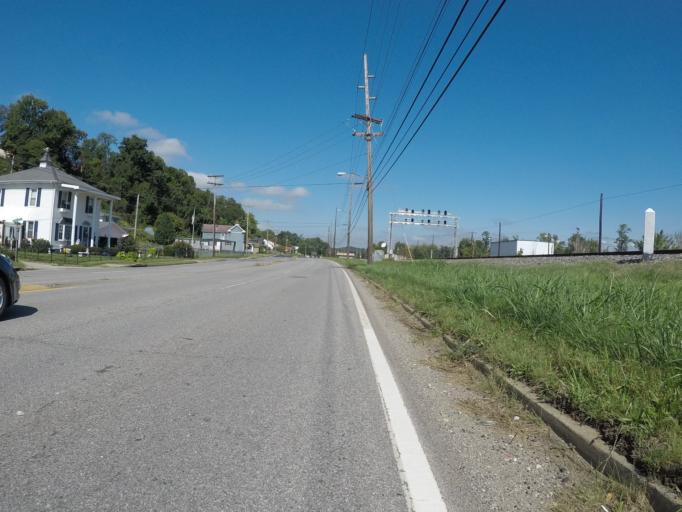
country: US
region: Ohio
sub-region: Lawrence County
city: South Point
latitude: 38.4321
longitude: -82.6046
